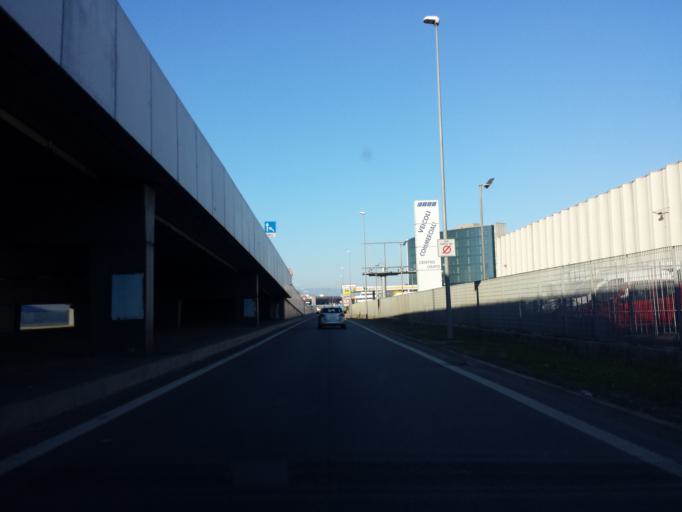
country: IT
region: Veneto
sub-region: Provincia di Vicenza
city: Creazzo
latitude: 45.5265
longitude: 11.5086
